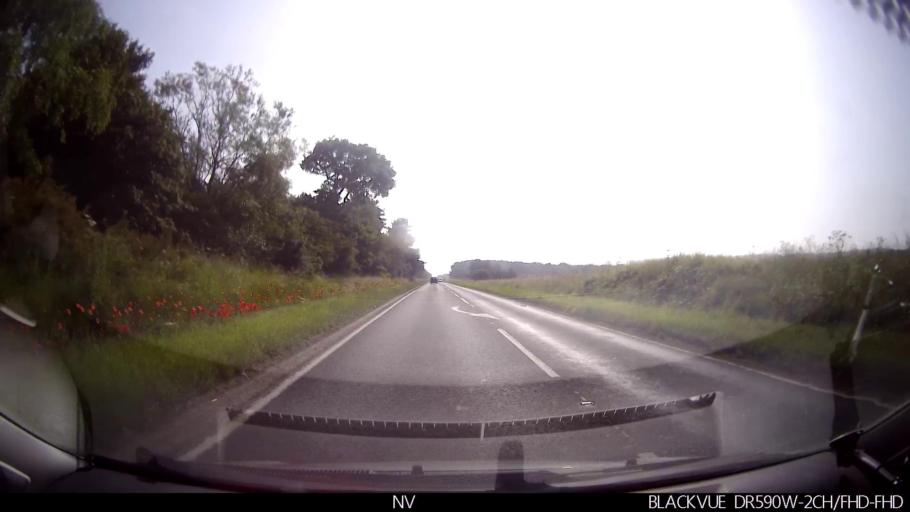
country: GB
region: England
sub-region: North Yorkshire
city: East Ayton
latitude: 54.1783
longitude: -0.5255
